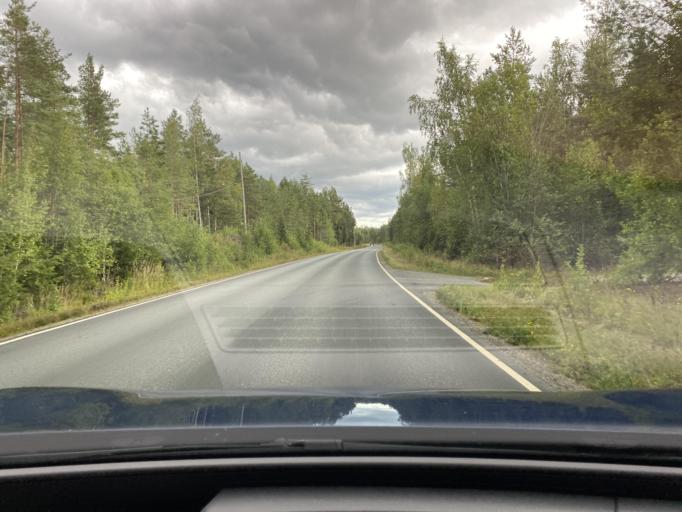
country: FI
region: Pirkanmaa
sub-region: Lounais-Pirkanmaa
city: Vammala
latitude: 61.3044
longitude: 22.9363
